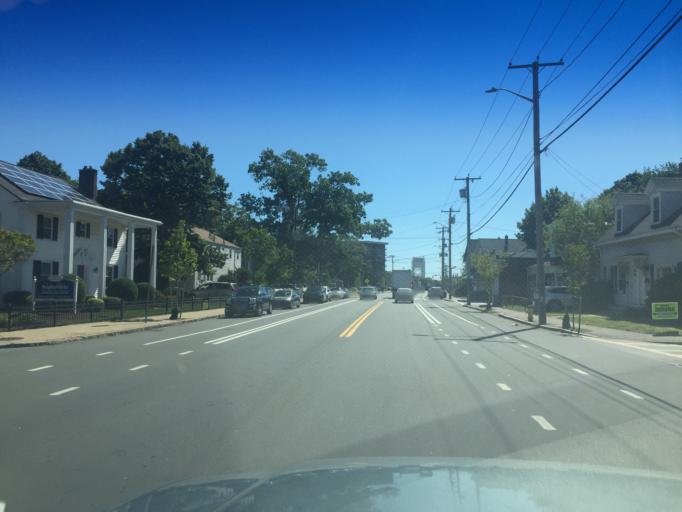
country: US
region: Massachusetts
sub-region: Norfolk County
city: Quincy
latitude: 42.2488
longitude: -70.9852
